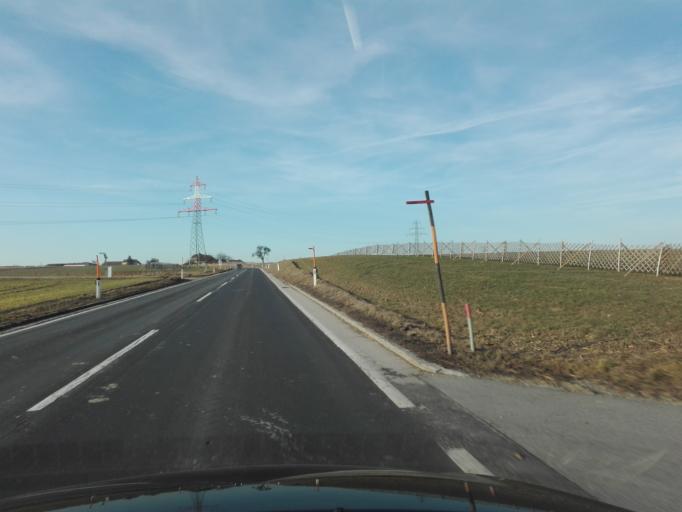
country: AT
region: Lower Austria
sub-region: Politischer Bezirk Amstetten
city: Strengberg
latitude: 48.1515
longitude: 14.6242
